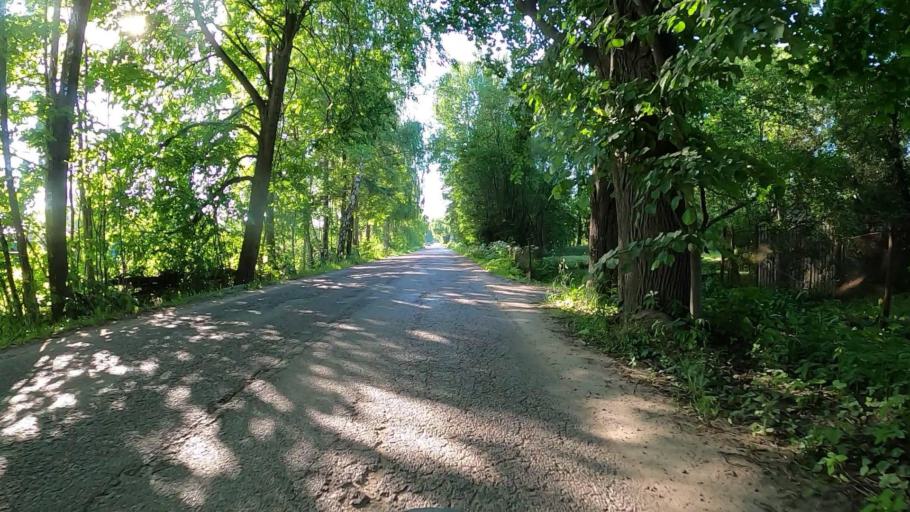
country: LV
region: Kekava
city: Kekava
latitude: 56.8827
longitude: 24.2585
